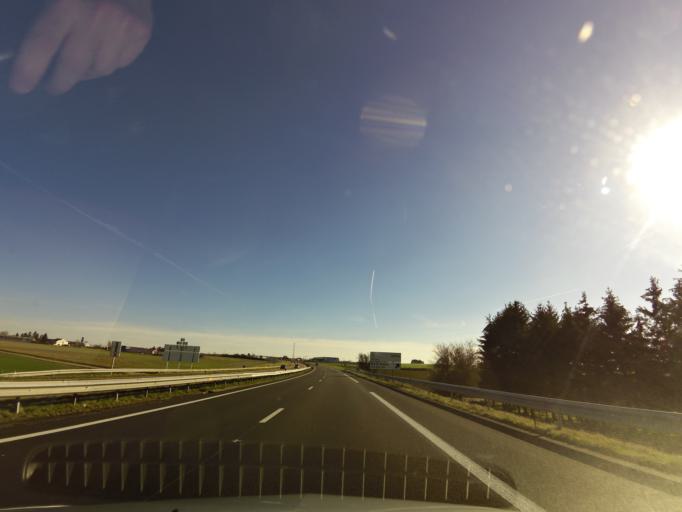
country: FR
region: Bourgogne
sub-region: Departement de l'Yonne
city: Joux-la-Ville
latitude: 47.6674
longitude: 3.8693
